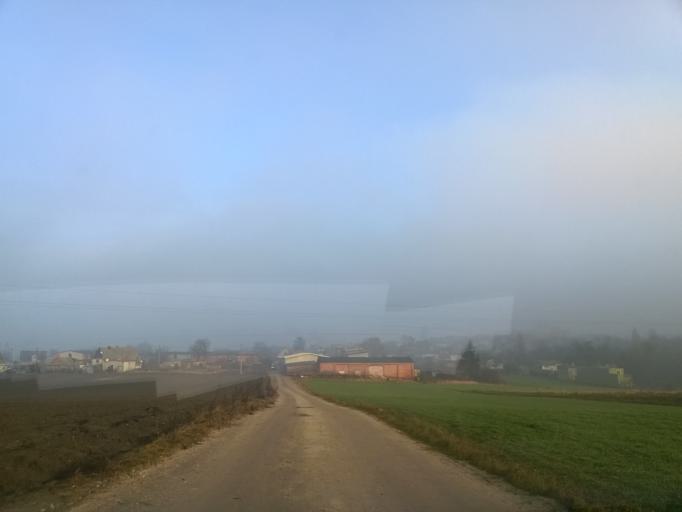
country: PL
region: Kujawsko-Pomorskie
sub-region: Powiat nakielski
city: Kcynia
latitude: 52.9868
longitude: 17.4826
